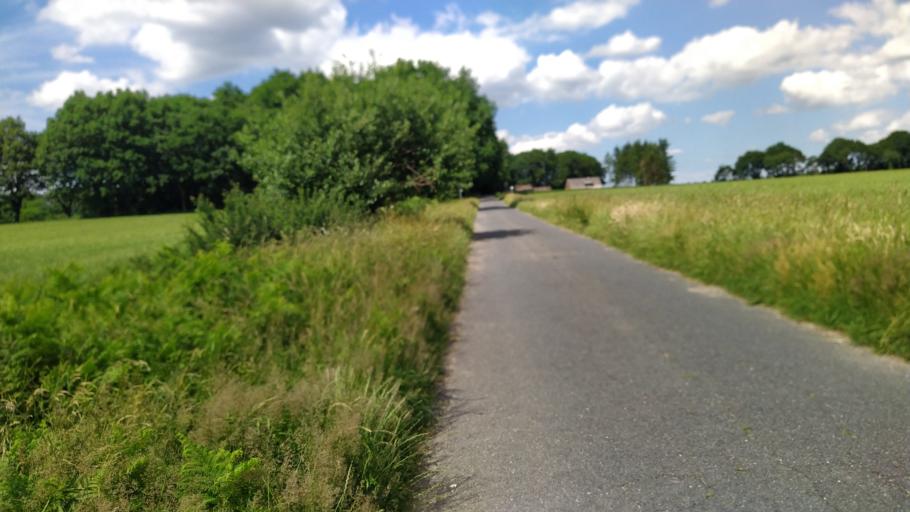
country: DE
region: Lower Saxony
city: Armstorf
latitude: 53.6025
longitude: 9.0764
